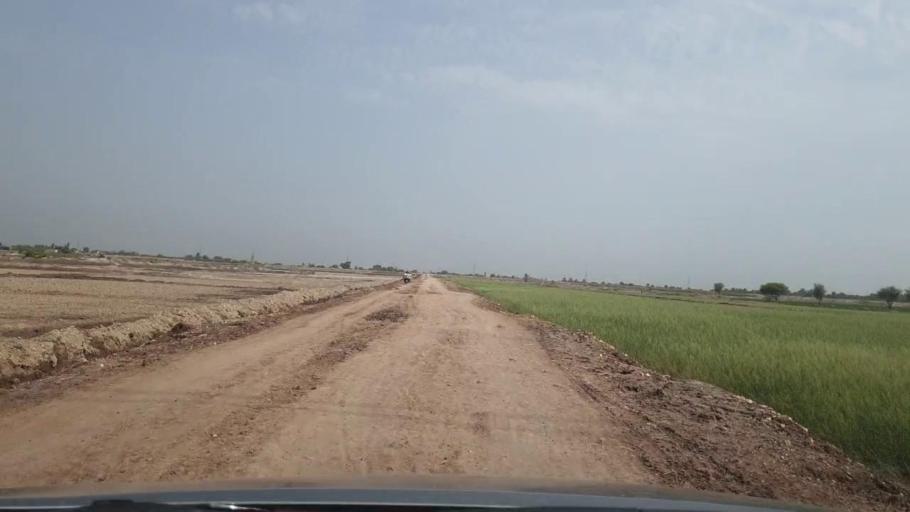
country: PK
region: Sindh
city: Rohri
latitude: 27.6742
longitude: 69.0262
